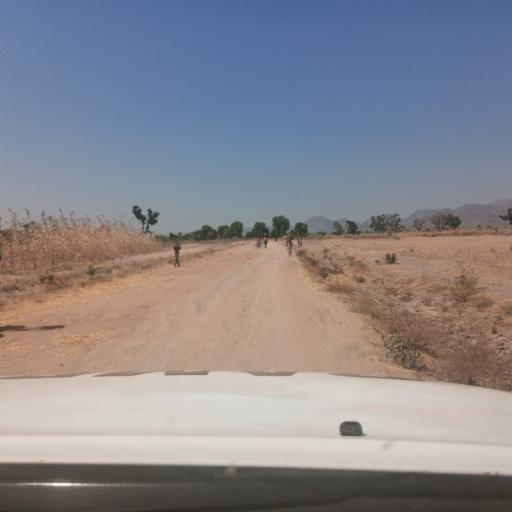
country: NG
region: Adamawa
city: Little Gombi
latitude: 9.7769
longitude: 12.5856
